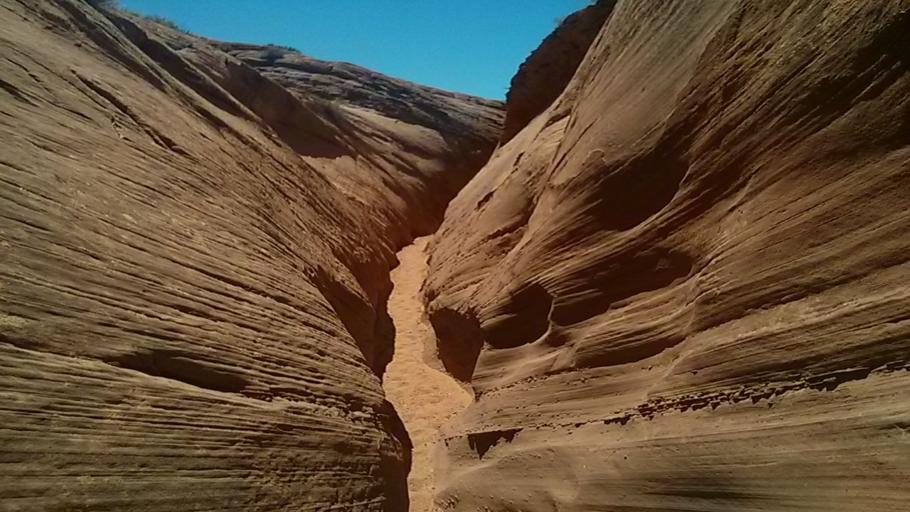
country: US
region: Arizona
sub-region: Coconino County
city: Page
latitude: 37.4850
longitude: -111.2093
